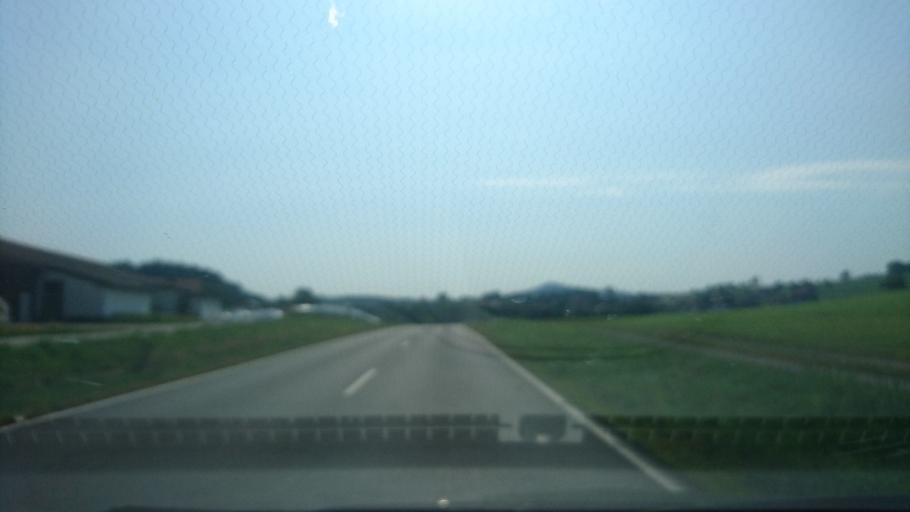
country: DE
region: Bavaria
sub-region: Lower Bavaria
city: Grafenau
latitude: 48.8768
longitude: 13.4015
